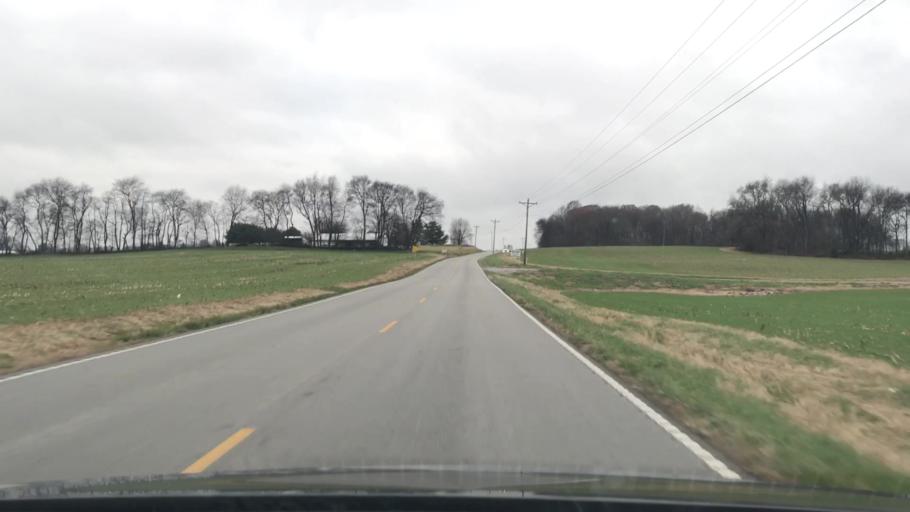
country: US
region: Kentucky
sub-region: Todd County
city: Guthrie
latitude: 36.6821
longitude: -87.2003
